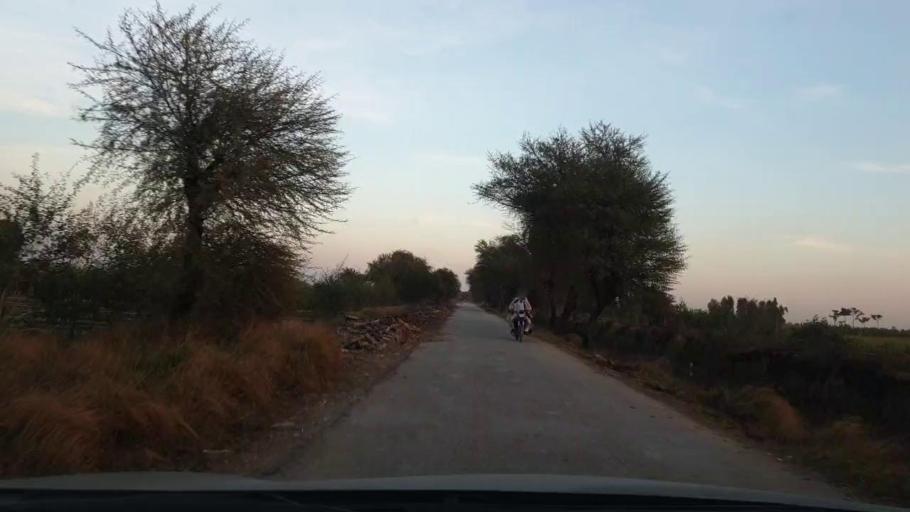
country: PK
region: Sindh
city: Tando Allahyar
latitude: 25.5917
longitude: 68.7101
